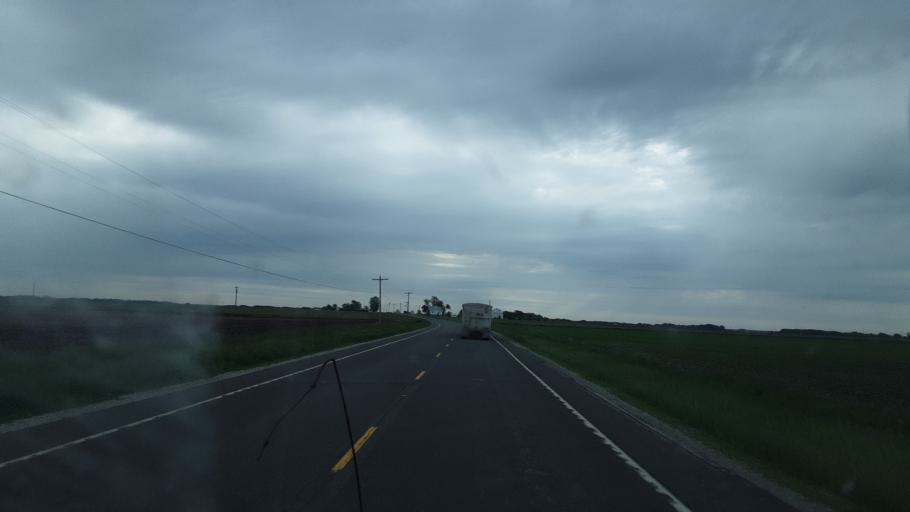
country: US
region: Illinois
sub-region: Fulton County
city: Lewistown
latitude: 40.3414
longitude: -90.2593
